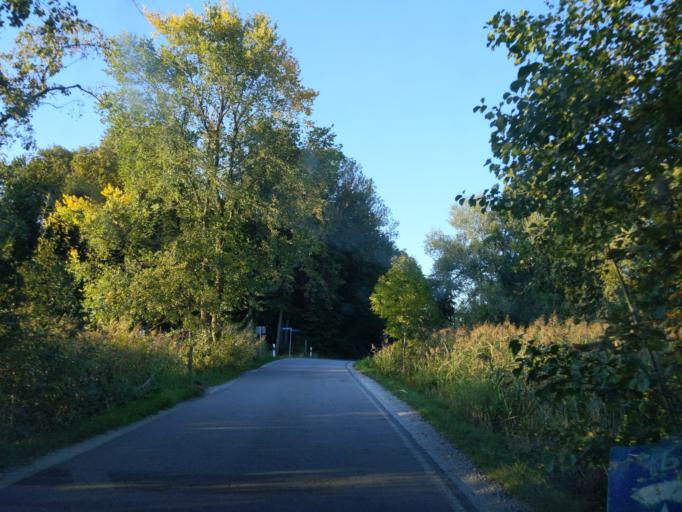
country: DE
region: Saxony
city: Guttau
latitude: 51.2710
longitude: 14.5694
